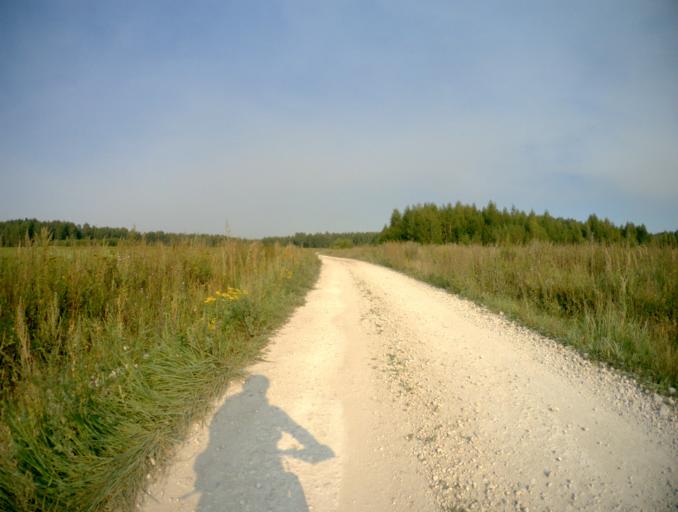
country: RU
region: Vladimir
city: Kosterevo
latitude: 55.9288
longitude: 39.5392
